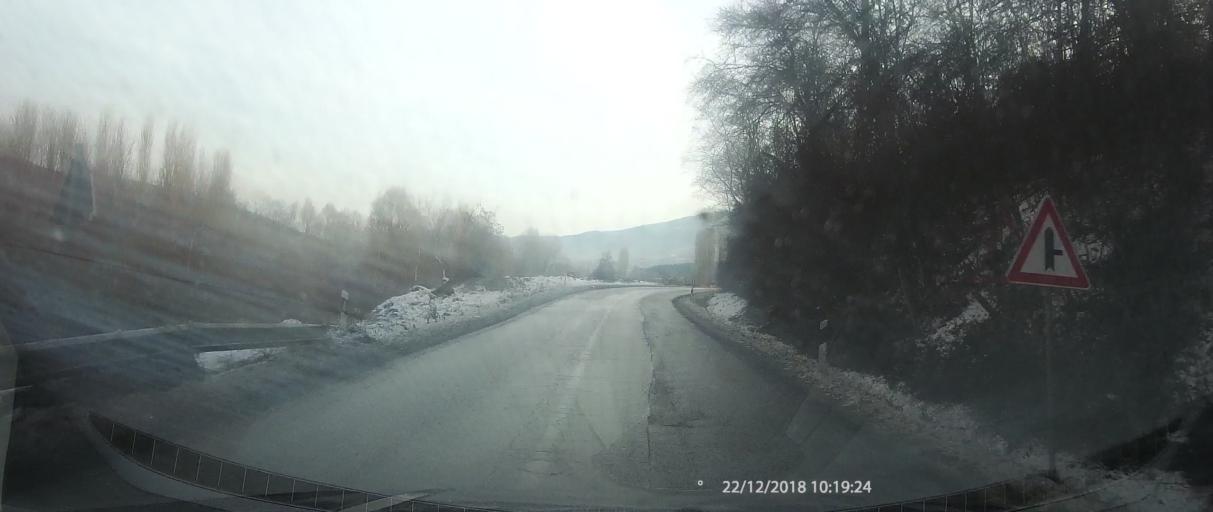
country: MK
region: Kriva Palanka
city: Kriva Palanka
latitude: 42.1893
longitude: 22.2943
